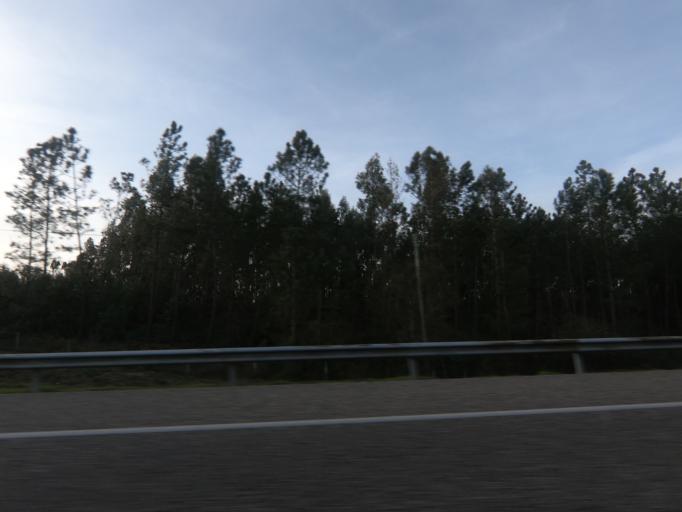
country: PT
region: Coimbra
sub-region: Soure
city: Soure
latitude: 39.9968
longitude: -8.6115
